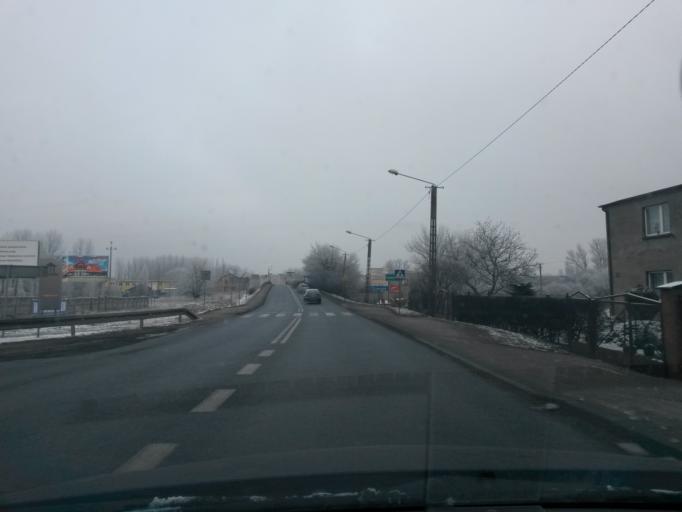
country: PL
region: Kujawsko-Pomorskie
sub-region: Powiat inowroclawski
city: Inowroclaw
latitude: 52.7453
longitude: 18.2535
